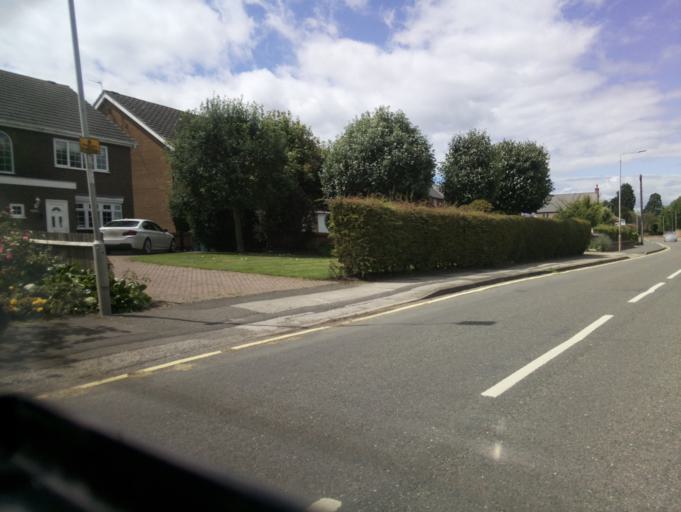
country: GB
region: England
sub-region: Nottinghamshire
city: Cotgrave
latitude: 52.8710
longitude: -1.0852
